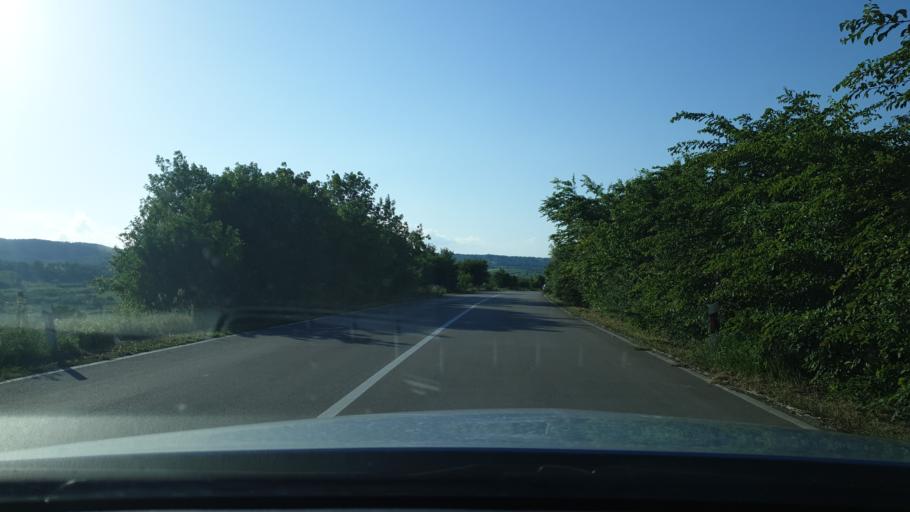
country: RS
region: Central Serbia
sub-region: Nisavski Okrug
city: Razanj
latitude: 43.6364
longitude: 21.5595
